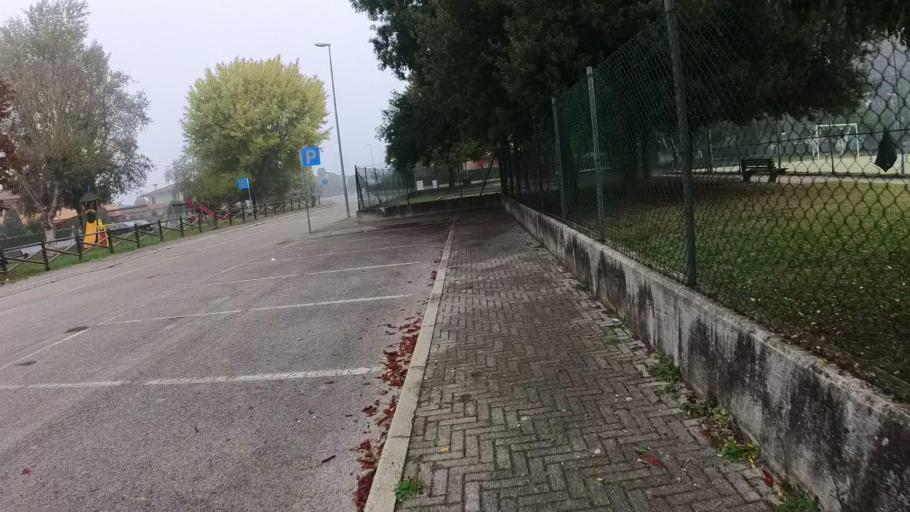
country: IT
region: Veneto
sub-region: Provincia di Venezia
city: Fosso
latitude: 45.3639
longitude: 12.0429
